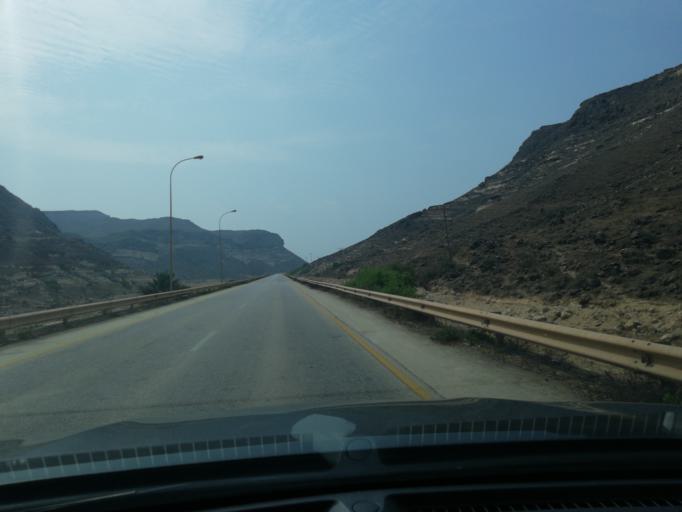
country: OM
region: Zufar
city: Salalah
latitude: 16.8948
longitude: 53.8168
